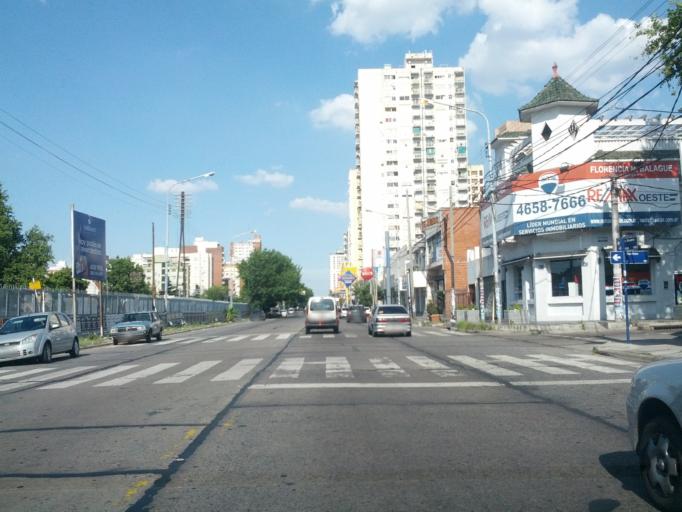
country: AR
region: Buenos Aires
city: San Justo
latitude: -34.6419
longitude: -58.5721
